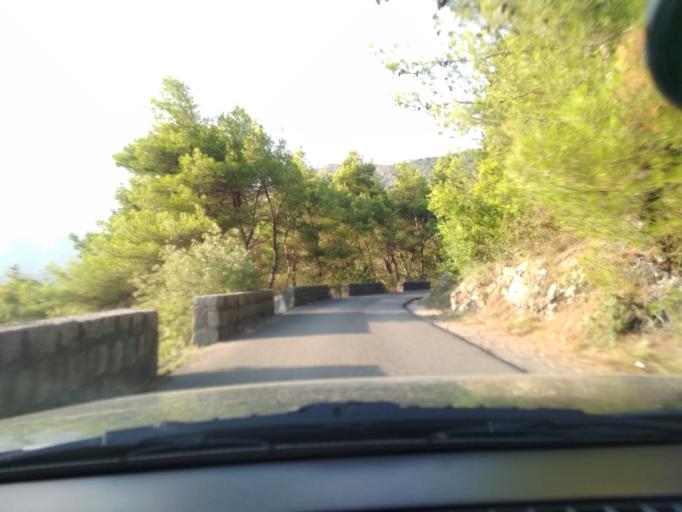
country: ME
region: Kotor
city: Kotor
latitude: 42.3989
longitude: 18.7595
